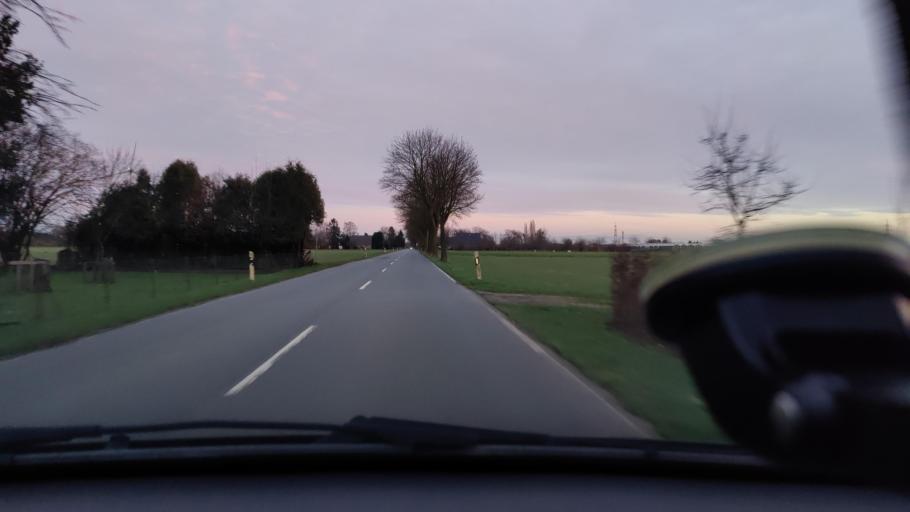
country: DE
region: North Rhine-Westphalia
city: Kalkar
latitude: 51.7160
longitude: 6.2739
